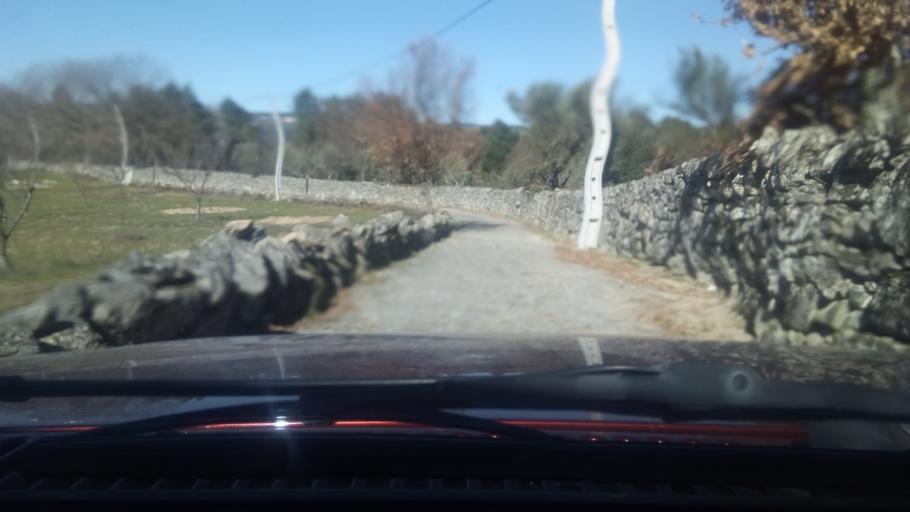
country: PT
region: Guarda
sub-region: Fornos de Algodres
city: Fornos de Algodres
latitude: 40.6082
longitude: -7.5007
